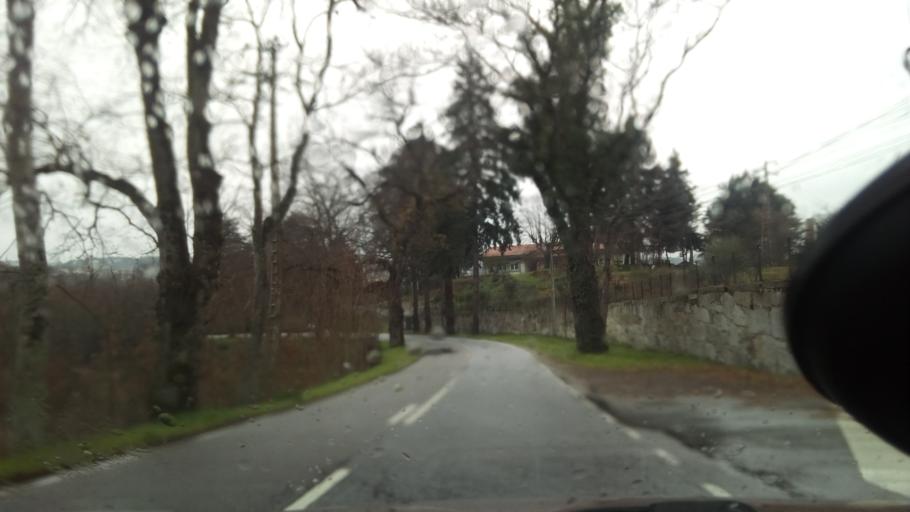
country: PT
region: Viseu
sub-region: Viseu
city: Rio de Loba
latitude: 40.6359
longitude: -7.8262
